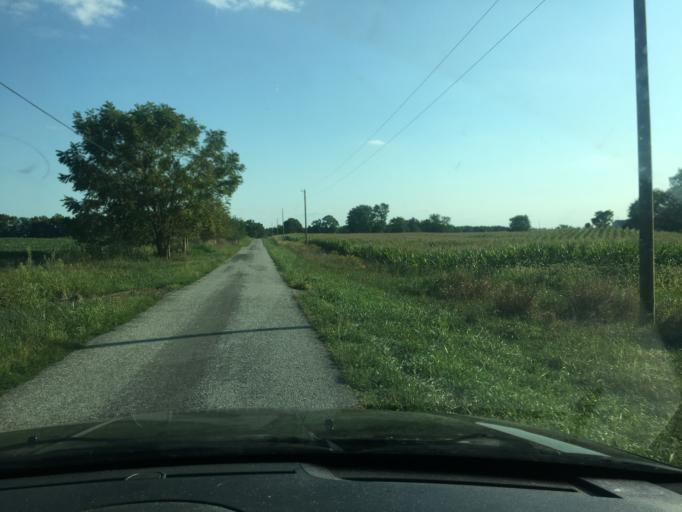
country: US
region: Ohio
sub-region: Logan County
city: West Liberty
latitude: 40.2347
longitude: -83.7865
